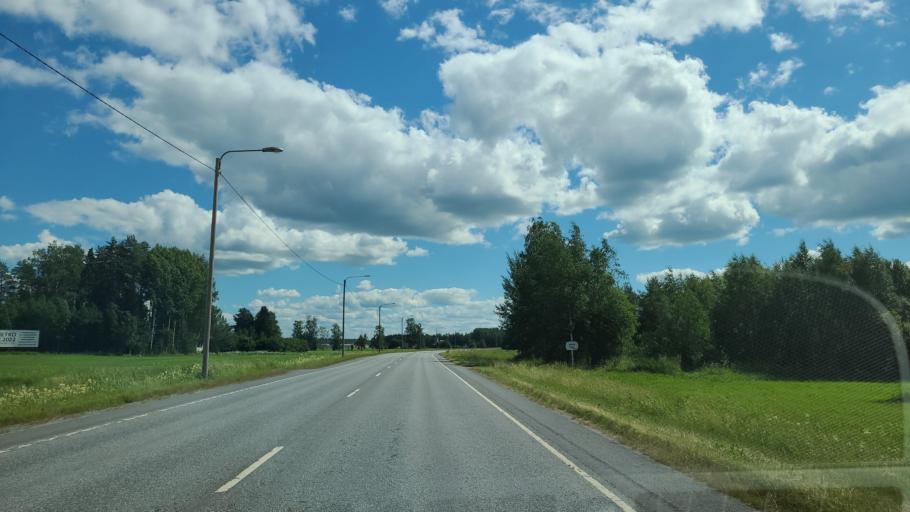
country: FI
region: Southern Ostrobothnia
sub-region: Seinaejoki
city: Ylistaro
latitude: 62.9146
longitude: 22.5723
